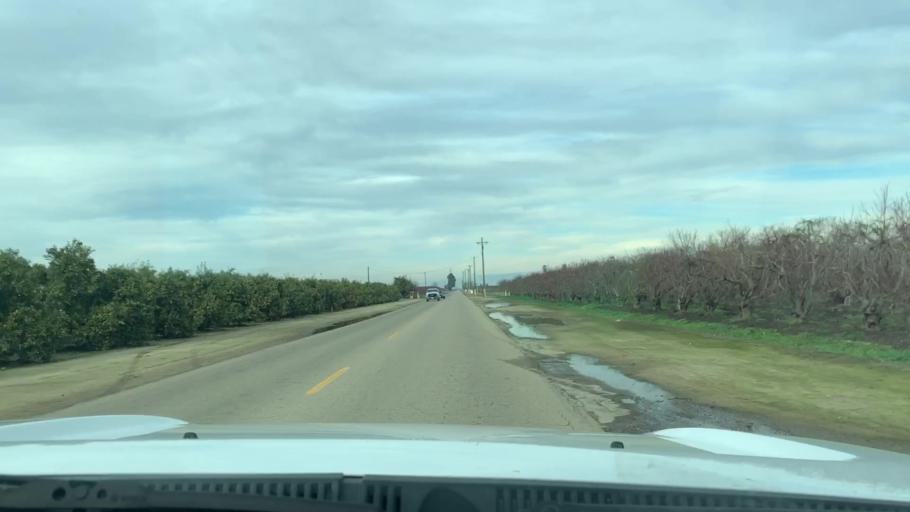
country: US
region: California
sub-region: Fresno County
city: Parlier
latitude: 36.6109
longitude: -119.5748
